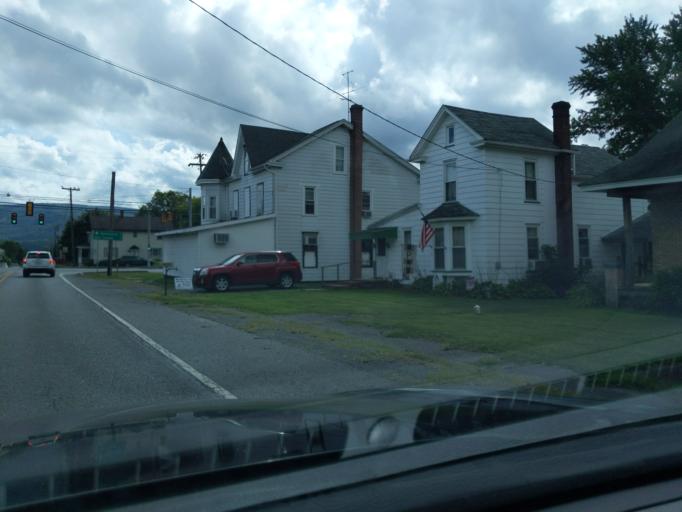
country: US
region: Pennsylvania
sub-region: Blair County
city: Duncansville
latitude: 40.3937
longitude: -78.4368
